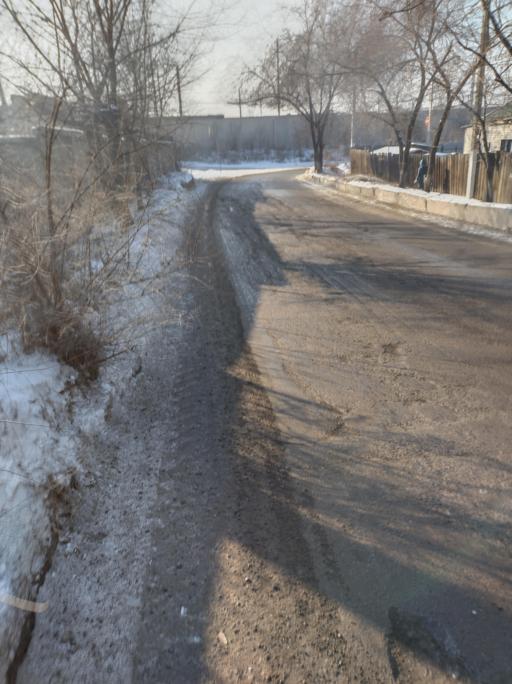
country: RU
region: Transbaikal Territory
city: Chita
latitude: 52.0249
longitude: 113.5051
